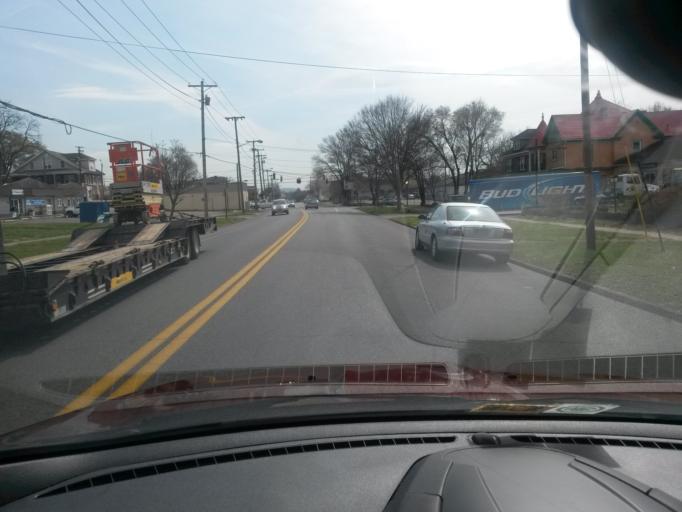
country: US
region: Virginia
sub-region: City of Roanoke
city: Roanoke
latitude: 37.2727
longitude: -79.9646
